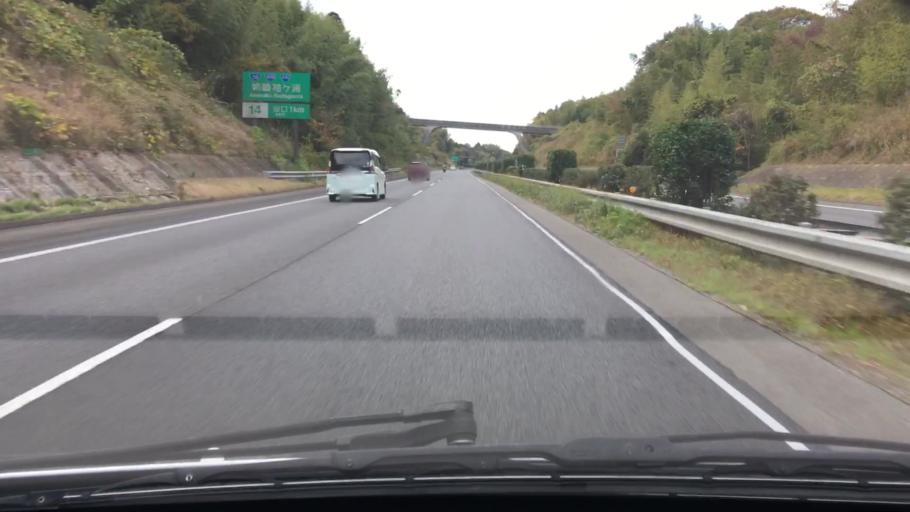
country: JP
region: Chiba
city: Ichihara
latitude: 35.4353
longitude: 140.0524
